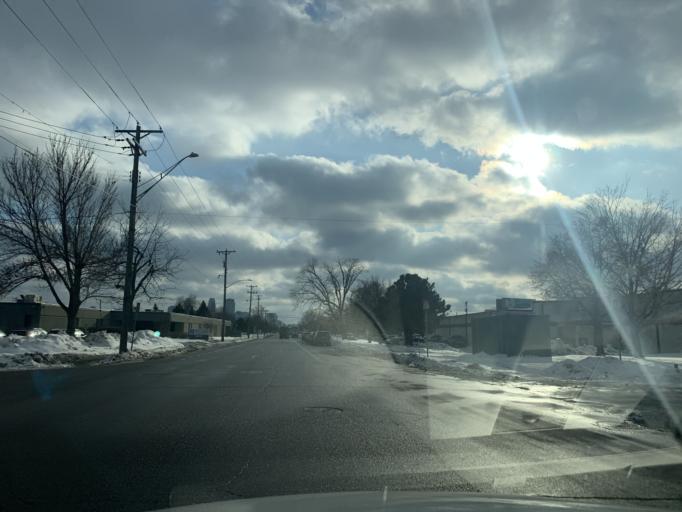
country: US
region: Minnesota
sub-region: Anoka County
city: Columbia Heights
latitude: 45.0122
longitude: -93.2806
